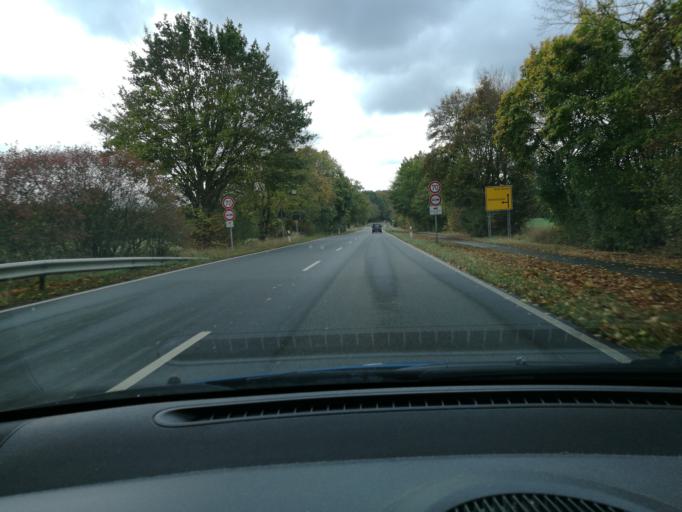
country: DE
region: Schleswig-Holstein
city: Gross Gronau
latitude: 53.7901
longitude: 10.7569
